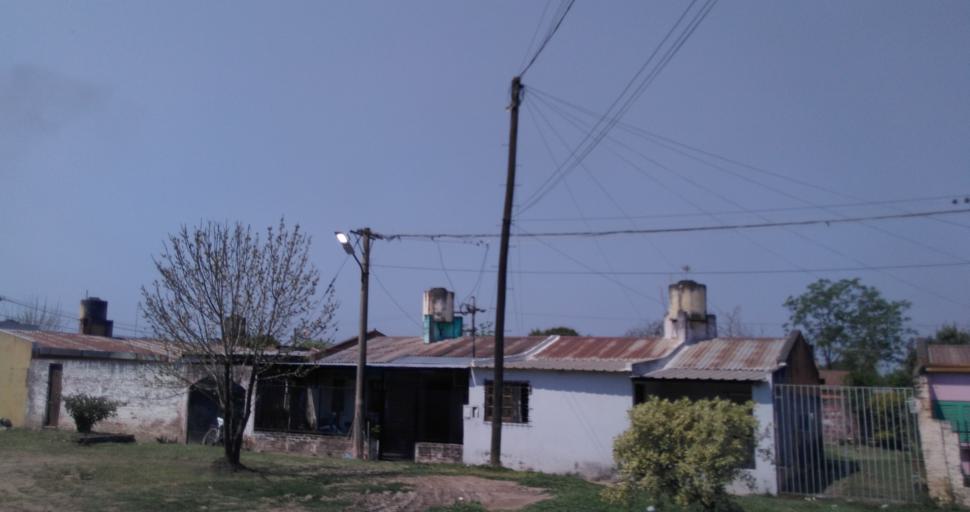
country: AR
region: Chaco
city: Fontana
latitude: -27.4221
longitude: -59.0249
